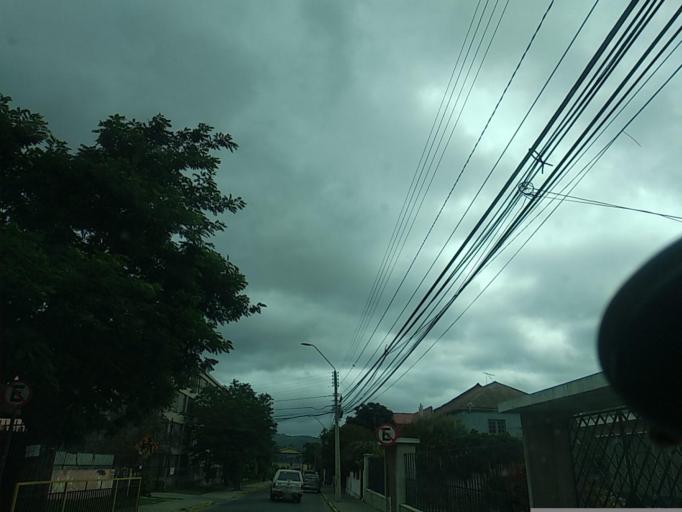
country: CL
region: Valparaiso
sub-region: Provincia de Marga Marga
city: Quilpue
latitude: -33.0495
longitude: -71.4456
